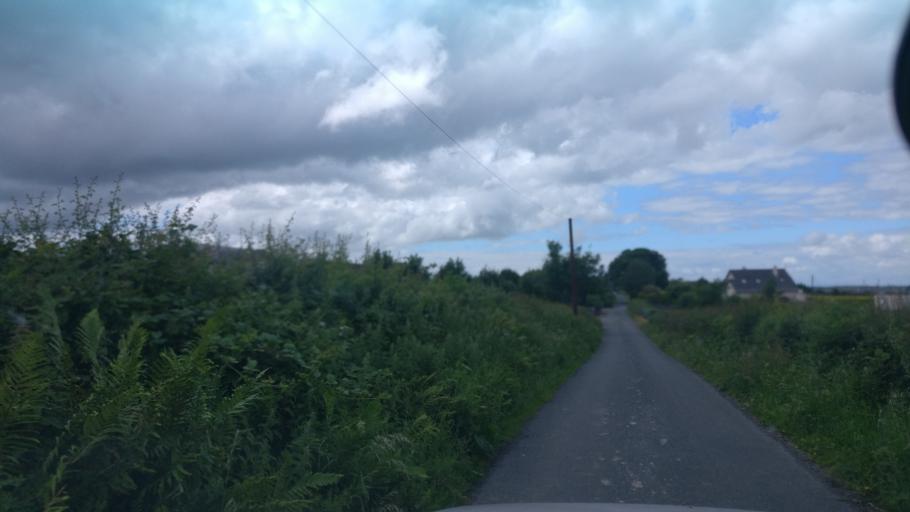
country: IE
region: Connaught
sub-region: County Galway
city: Loughrea
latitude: 53.1692
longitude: -8.5489
